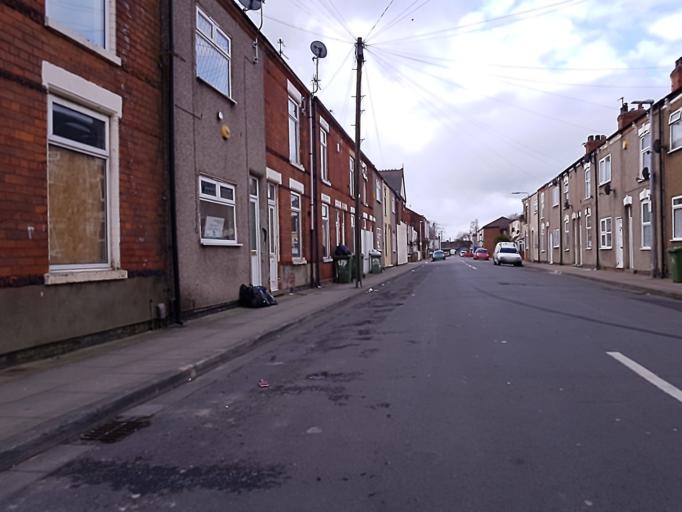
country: GB
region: England
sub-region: North East Lincolnshire
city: Grimsby
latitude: 53.5681
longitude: -0.0619
